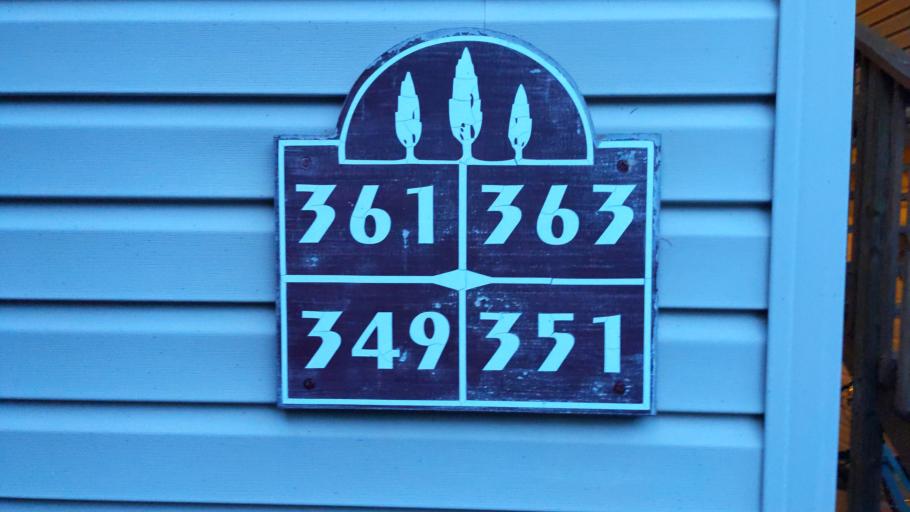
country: US
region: Virginia
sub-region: Montgomery County
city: Blacksburg
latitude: 37.2051
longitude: -80.3943
